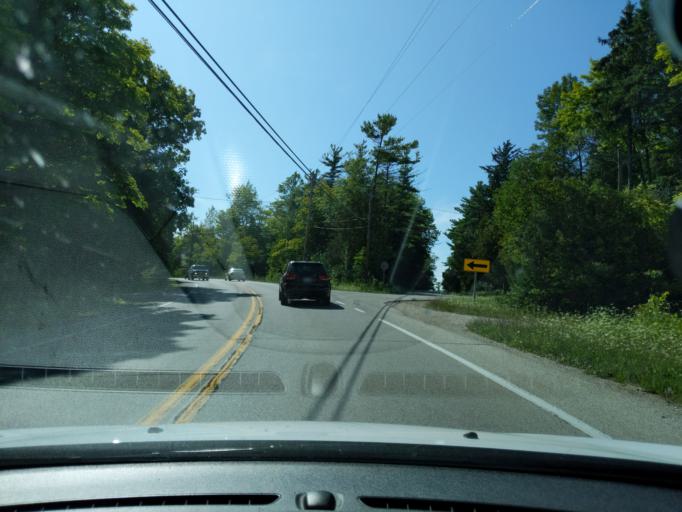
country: US
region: Michigan
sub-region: Delta County
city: Escanaba
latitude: 45.2590
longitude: -87.0665
